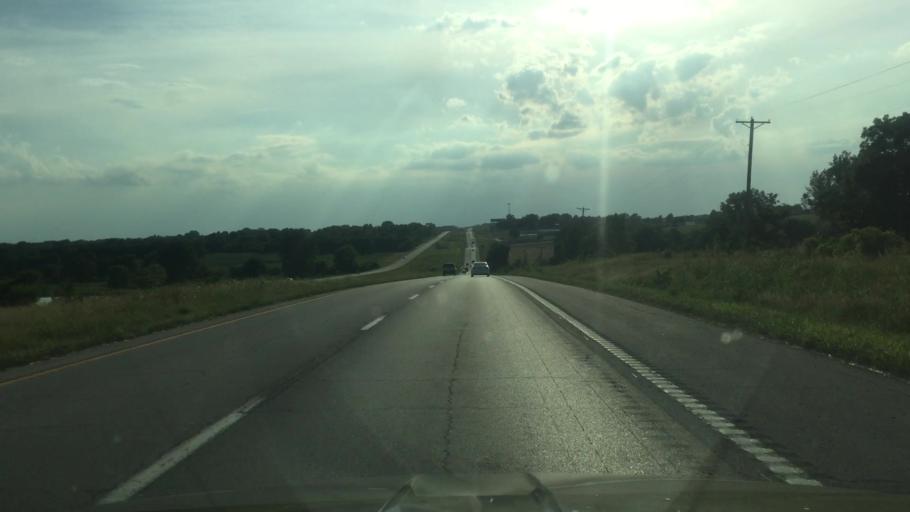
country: US
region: Missouri
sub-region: Jackson County
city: Lone Jack
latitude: 38.8693
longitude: -94.0959
